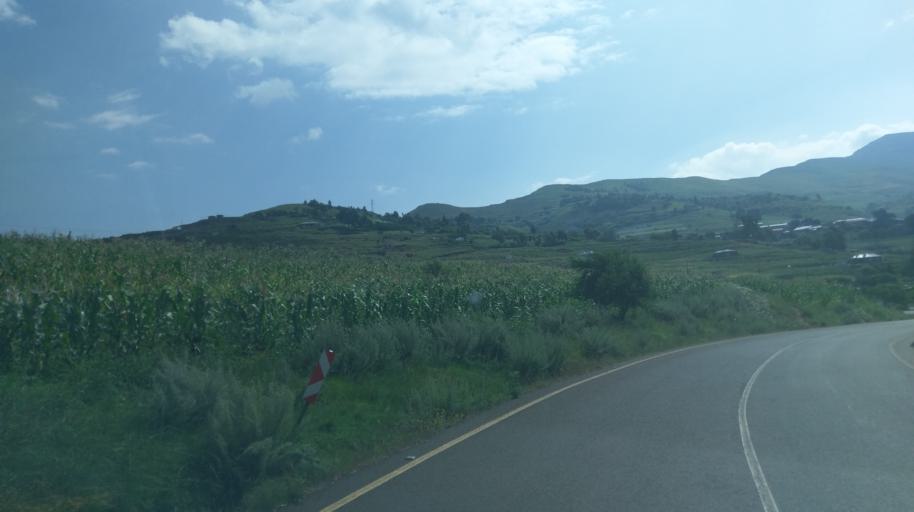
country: LS
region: Thaba-Tseka
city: Thaba-Tseka
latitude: -29.1447
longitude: 28.4907
